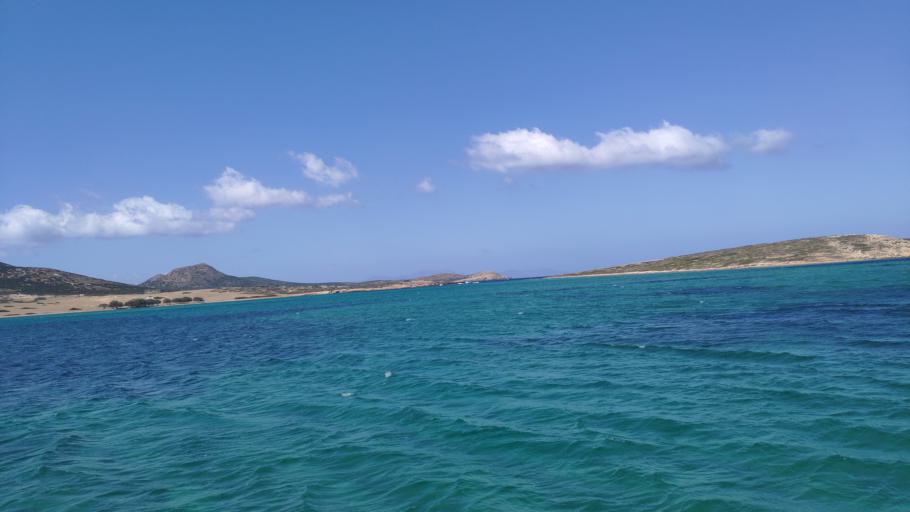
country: GR
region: South Aegean
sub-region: Nomos Kykladon
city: Antiparos
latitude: 36.9734
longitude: 25.0227
